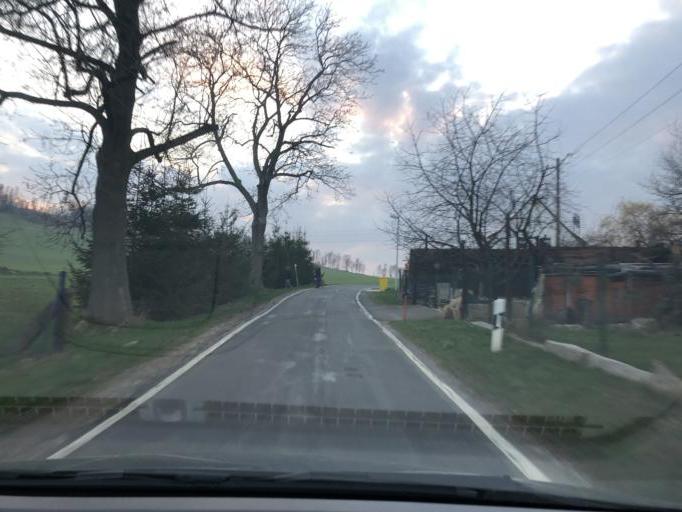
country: DE
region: Saxony
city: Kamenz
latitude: 51.2405
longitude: 14.0812
